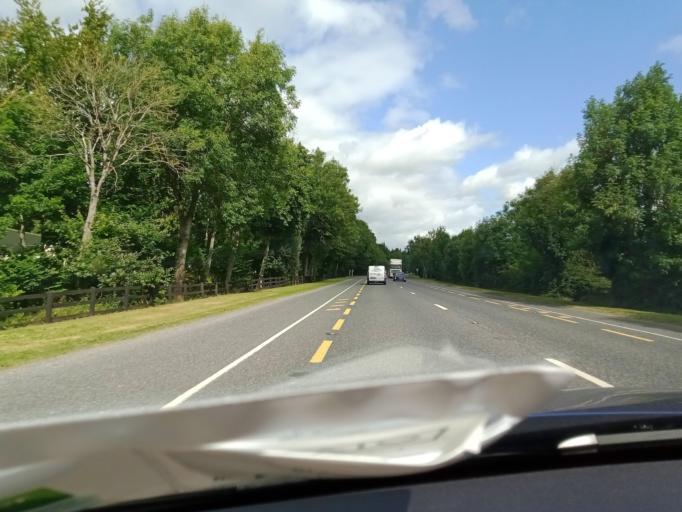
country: IE
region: Leinster
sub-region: Laois
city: Abbeyleix
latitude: 52.8866
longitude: -7.3646
